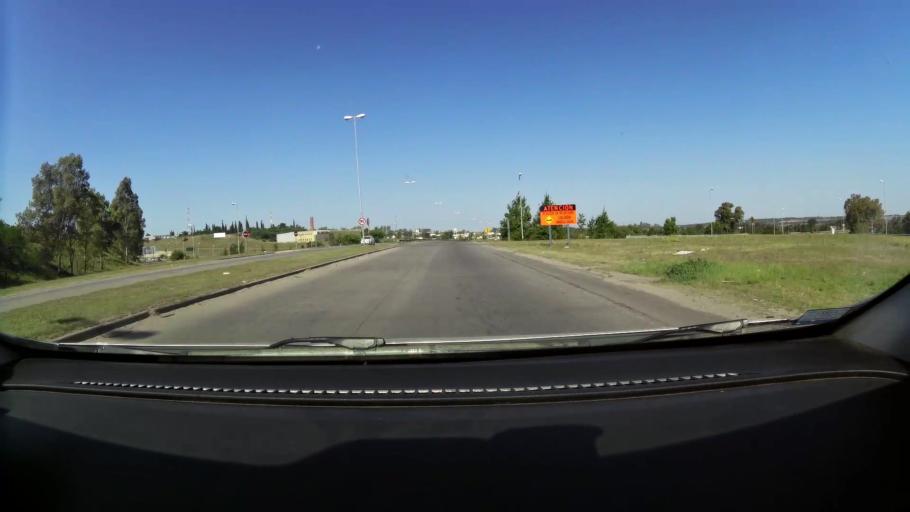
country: AR
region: Cordoba
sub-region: Departamento de Capital
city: Cordoba
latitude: -31.3978
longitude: -64.1306
